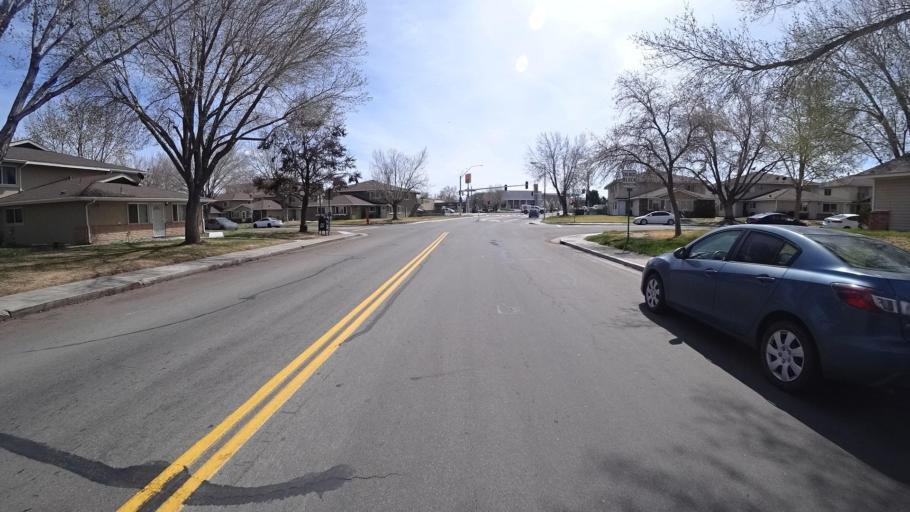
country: US
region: Nevada
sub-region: Washoe County
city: Reno
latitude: 39.4777
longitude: -119.7813
